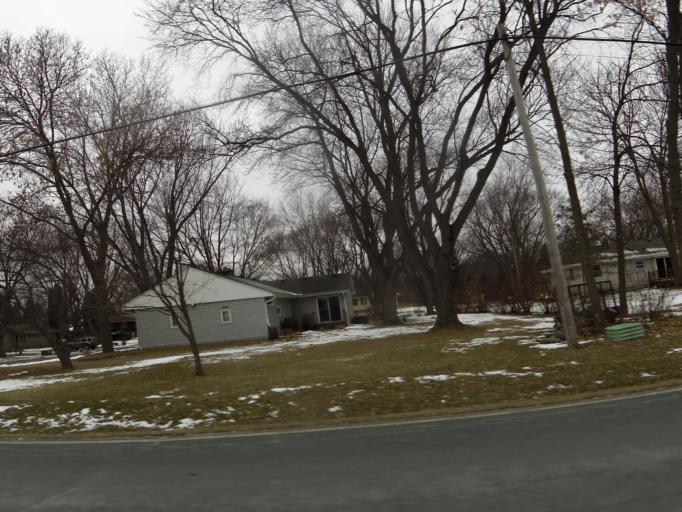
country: US
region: Minnesota
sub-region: Hennepin County
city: Long Lake
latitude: 45.0023
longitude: -93.5840
